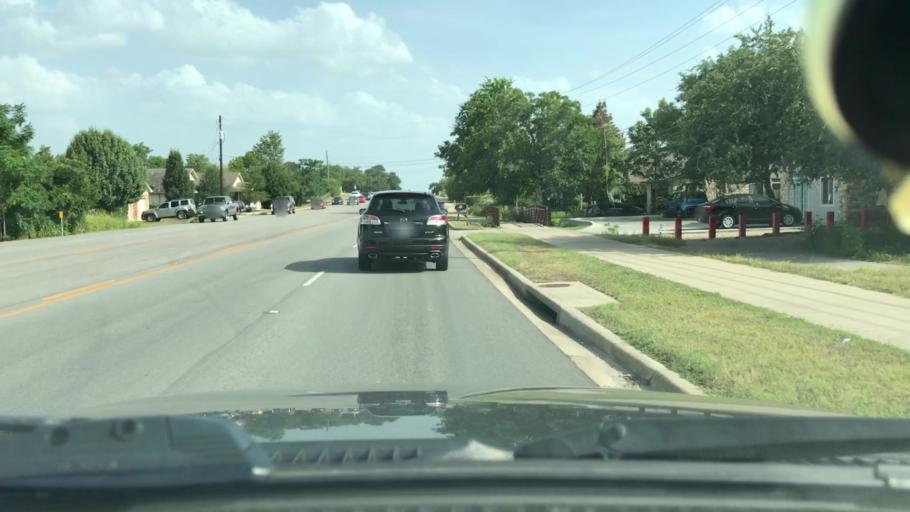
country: US
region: Texas
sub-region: Williamson County
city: Leander
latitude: 30.5462
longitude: -97.8519
